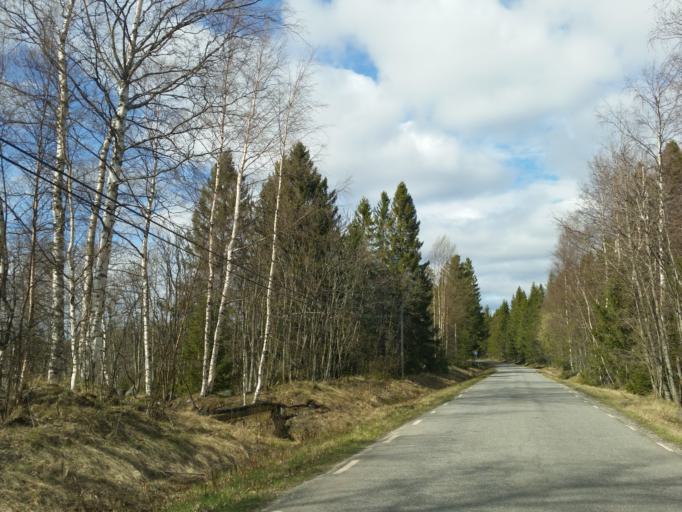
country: SE
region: Vaesterbotten
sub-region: Umea Kommun
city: Taftea
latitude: 63.7542
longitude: 20.5372
